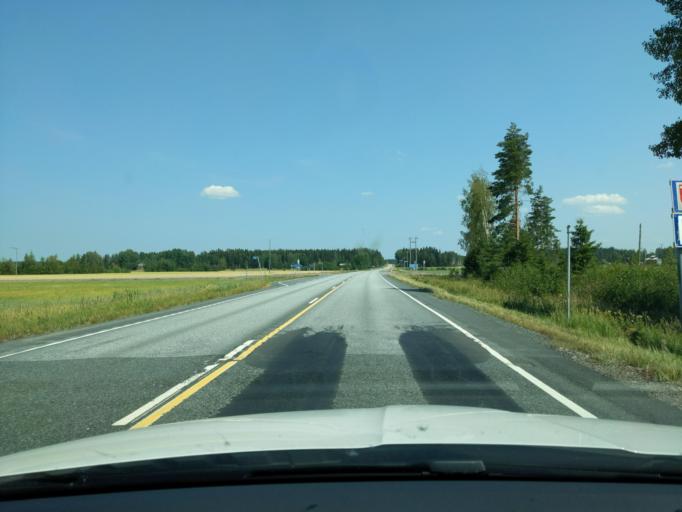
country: FI
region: Haeme
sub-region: Forssa
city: Ypaejae
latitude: 60.7316
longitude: 23.2485
